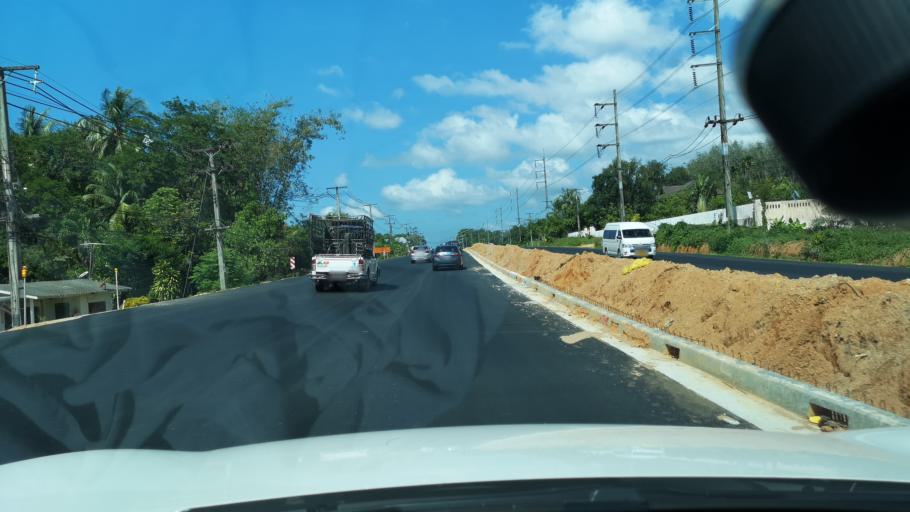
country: TH
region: Phangnga
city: Thai Mueang
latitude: 8.4219
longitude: 98.2588
